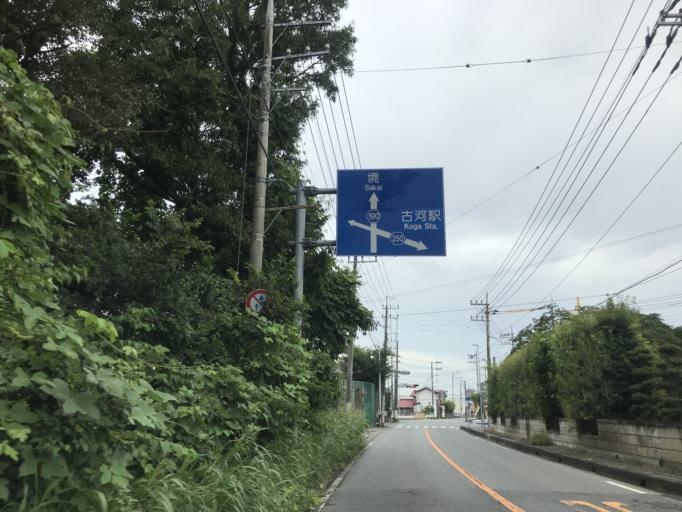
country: JP
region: Ibaraki
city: Koga
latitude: 36.1700
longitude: 139.7675
